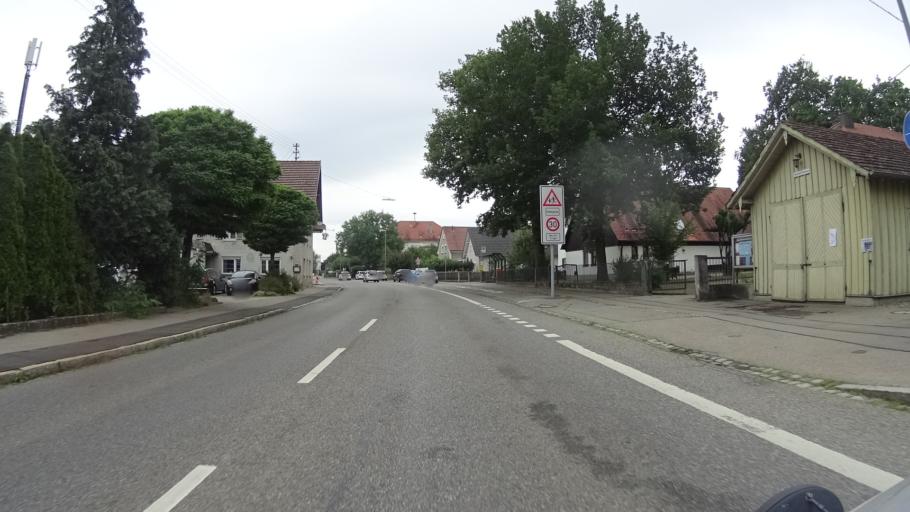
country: DE
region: Bavaria
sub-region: Swabia
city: Heimertingen
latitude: 48.0147
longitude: 10.1617
